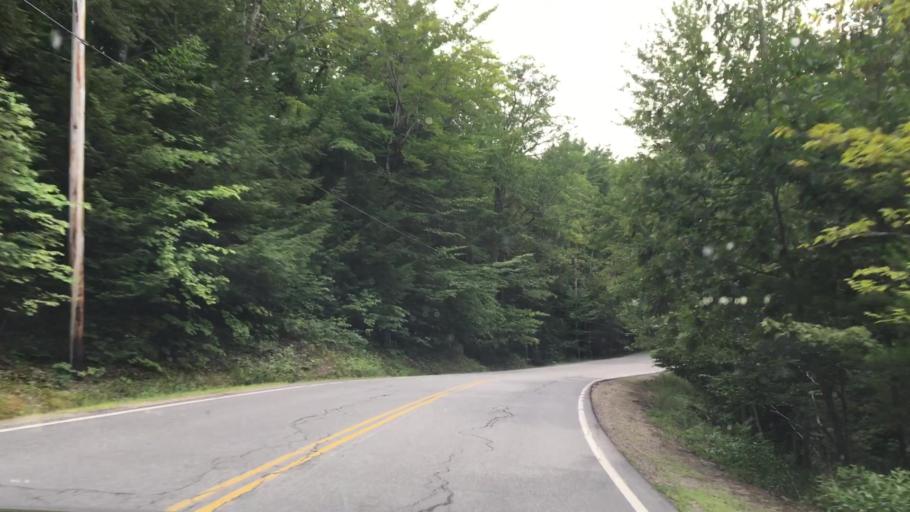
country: US
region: New Hampshire
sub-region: Carroll County
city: Center Harbor
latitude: 43.7030
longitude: -71.5022
